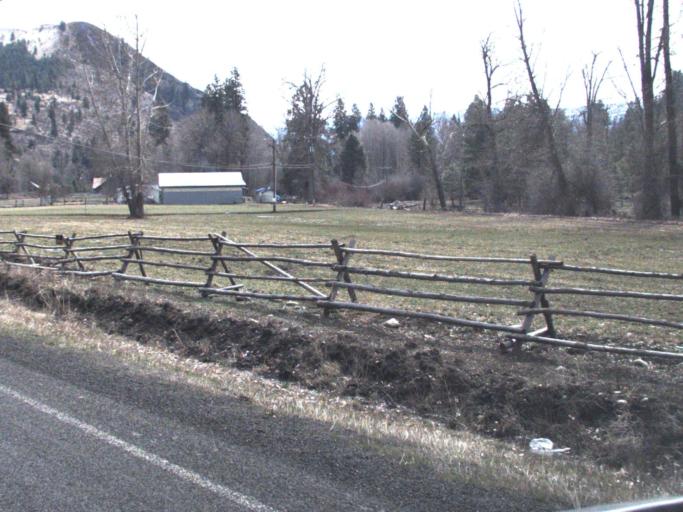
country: US
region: Washington
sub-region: Yakima County
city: Tieton
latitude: 46.8667
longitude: -120.9592
